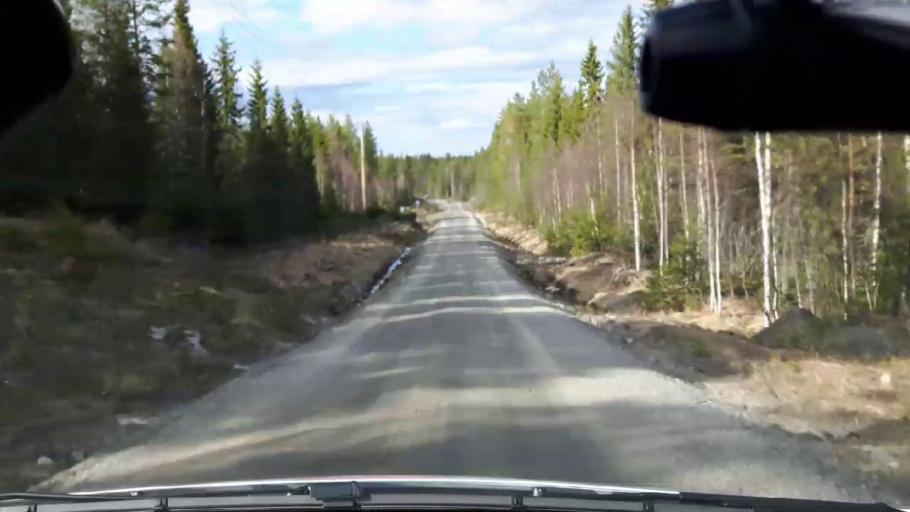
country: SE
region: Jaemtland
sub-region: Bergs Kommun
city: Hoverberg
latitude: 62.8703
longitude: 14.6646
